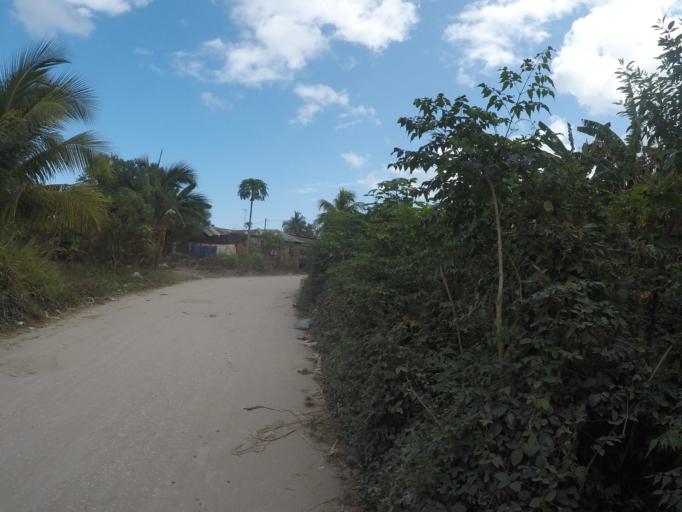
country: TZ
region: Zanzibar Urban/West
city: Zanzibar
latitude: -6.1856
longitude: 39.2126
